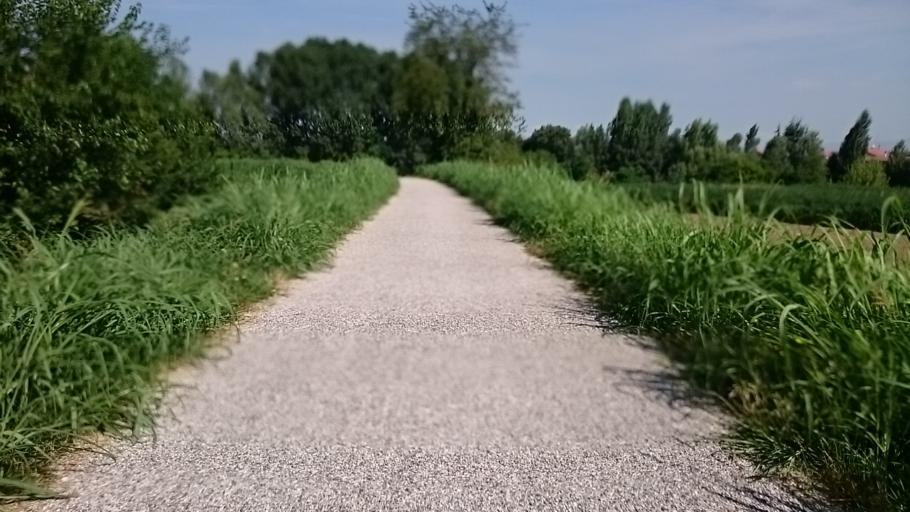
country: IT
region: Veneto
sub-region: Provincia di Padova
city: Tencarola
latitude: 45.3928
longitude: 11.8012
